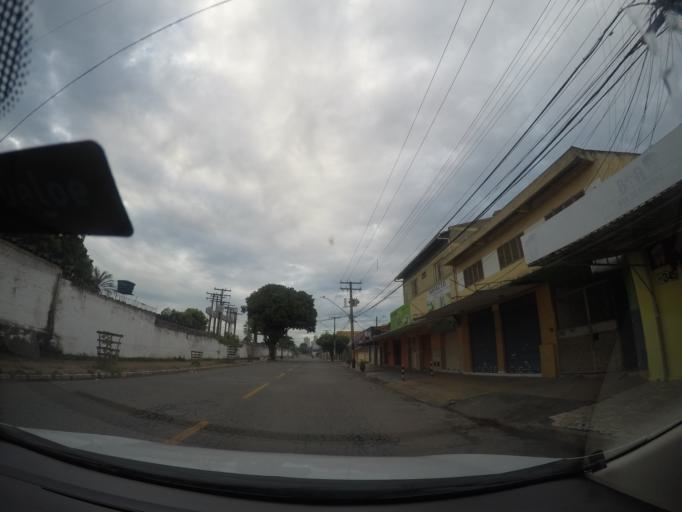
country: BR
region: Goias
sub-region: Goiania
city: Goiania
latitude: -16.6580
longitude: -49.2525
